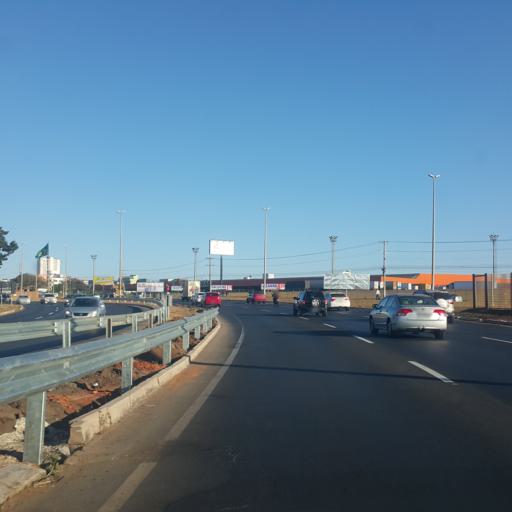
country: BR
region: Federal District
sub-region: Brasilia
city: Brasilia
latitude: -15.8349
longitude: -48.0774
